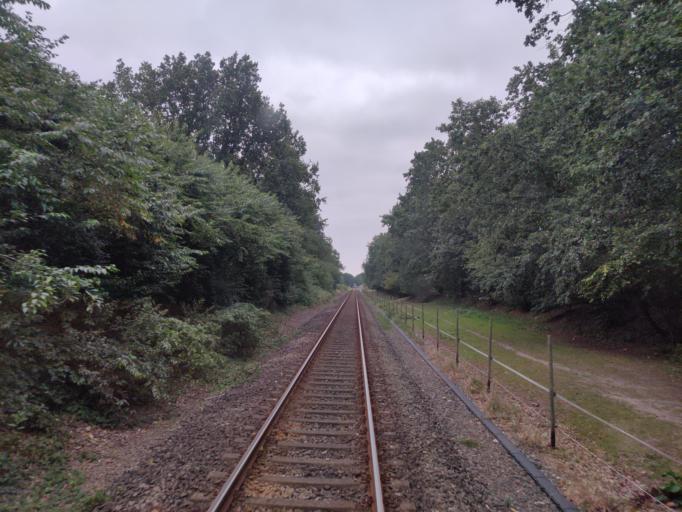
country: DE
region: Lower Saxony
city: Deinste
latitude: 53.5535
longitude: 9.4622
